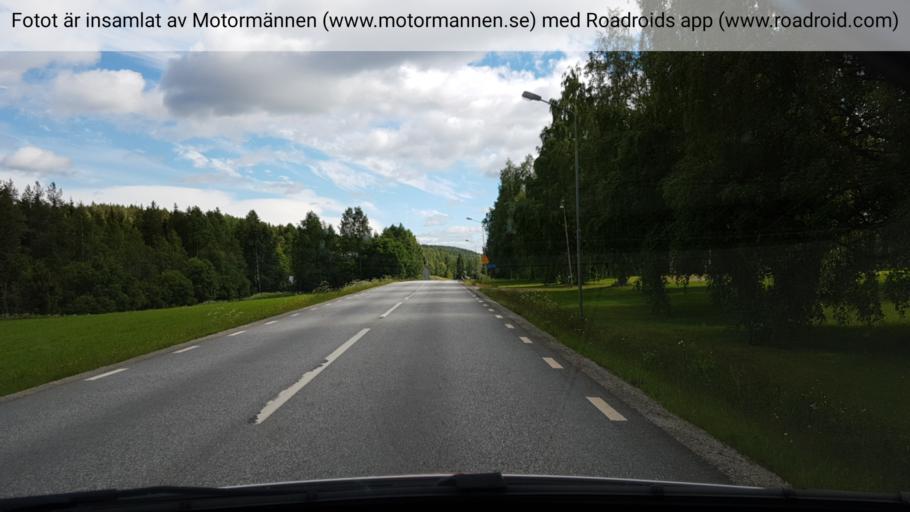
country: SE
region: Vaesterbotten
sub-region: Vindelns Kommun
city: Vindeln
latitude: 64.1583
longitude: 19.5044
